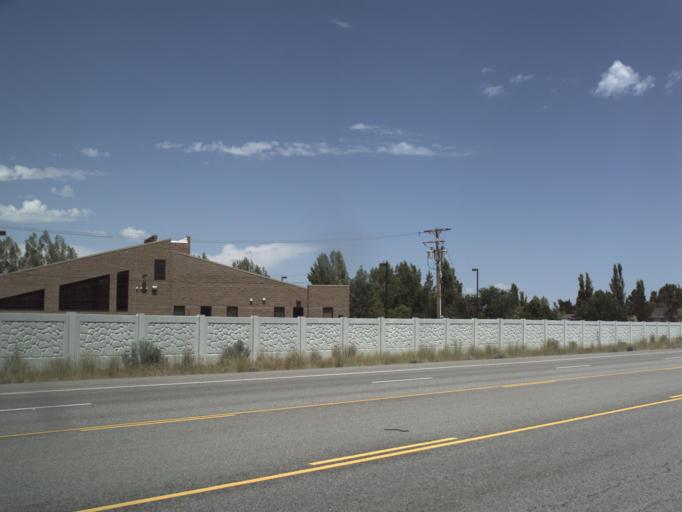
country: US
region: Utah
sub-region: Tooele County
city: Stansbury park
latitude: 40.6328
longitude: -112.2901
